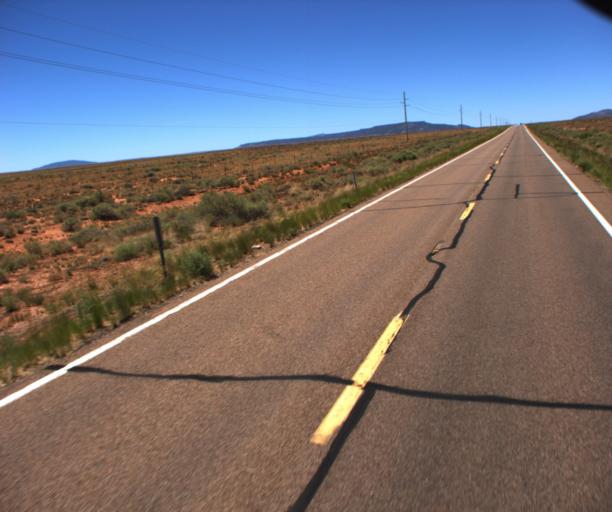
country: US
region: Arizona
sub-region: Coconino County
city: LeChee
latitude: 34.9494
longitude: -110.7642
